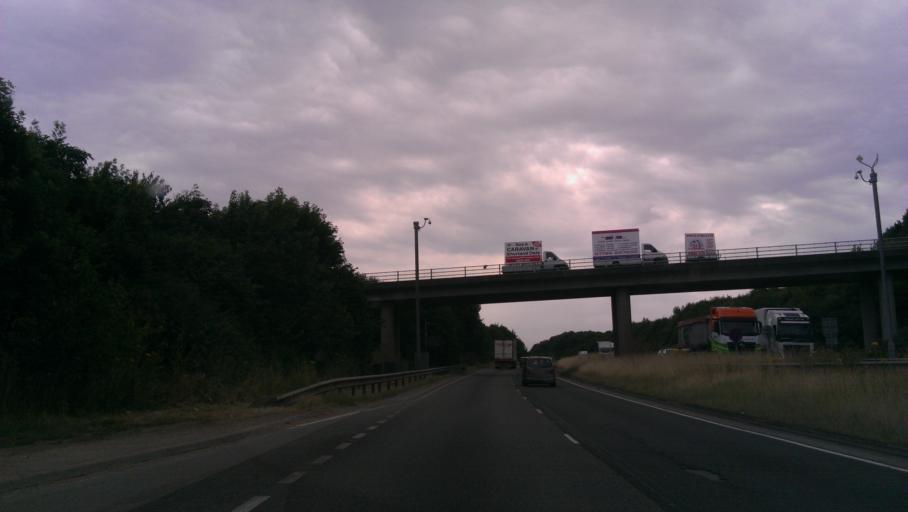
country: GB
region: England
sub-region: Kent
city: Newington
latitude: 51.3370
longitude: 0.6719
